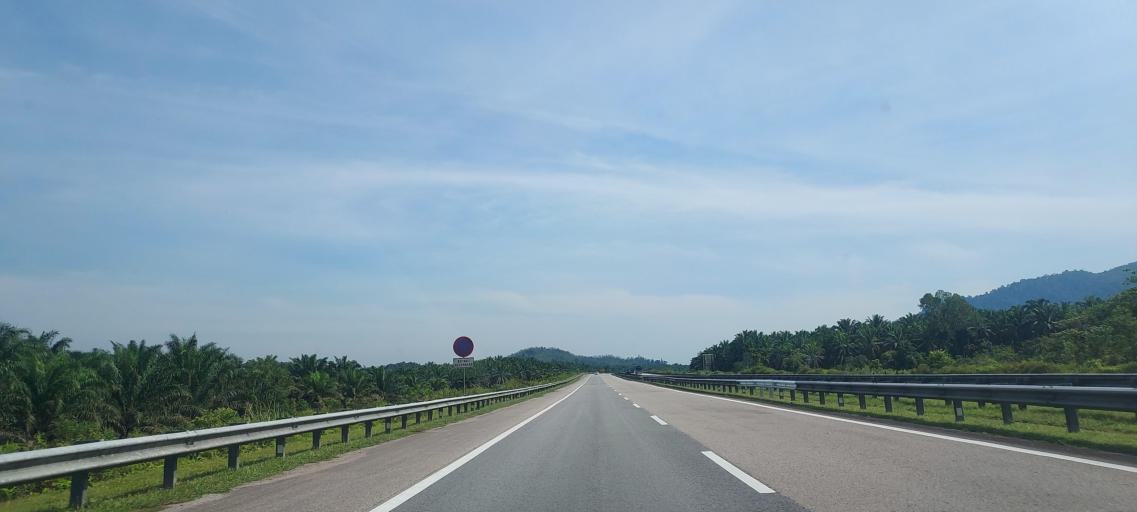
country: MY
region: Terengganu
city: Marang
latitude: 4.9600
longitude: 103.0825
